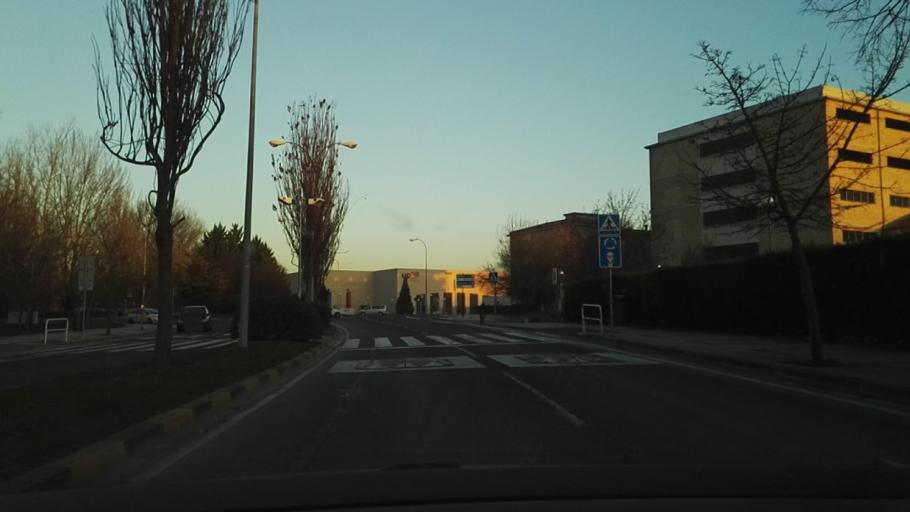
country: ES
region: Navarre
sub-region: Provincia de Navarra
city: Segundo Ensanche
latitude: 42.7964
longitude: -1.6325
